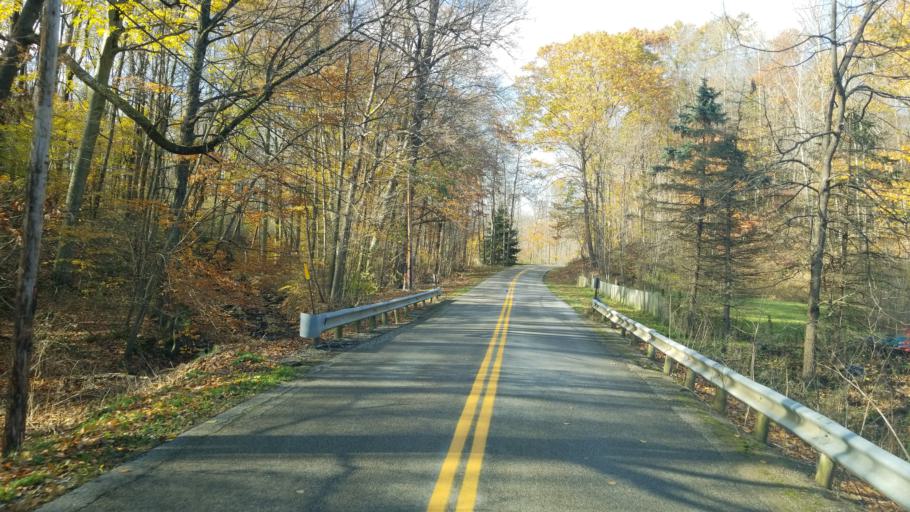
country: US
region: Ohio
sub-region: Sandusky County
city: Bellville
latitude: 40.6421
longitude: -82.4236
